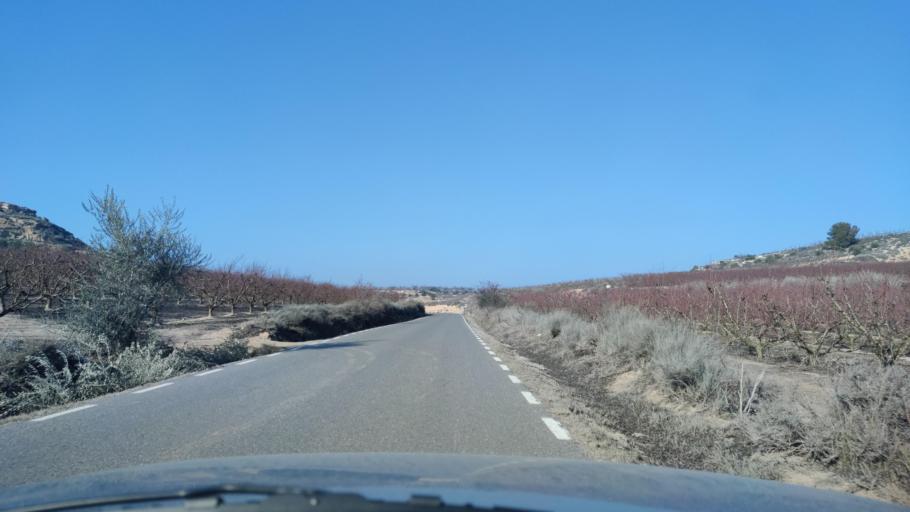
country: ES
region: Catalonia
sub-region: Provincia de Lleida
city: Sunyer
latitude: 41.5157
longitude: 0.5662
